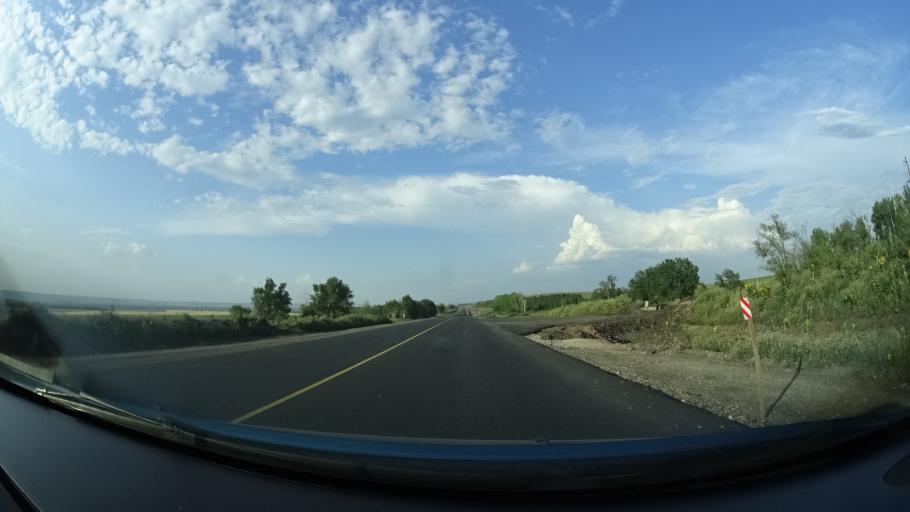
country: RU
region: Samara
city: Sukhodol
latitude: 53.7471
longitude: 50.8630
